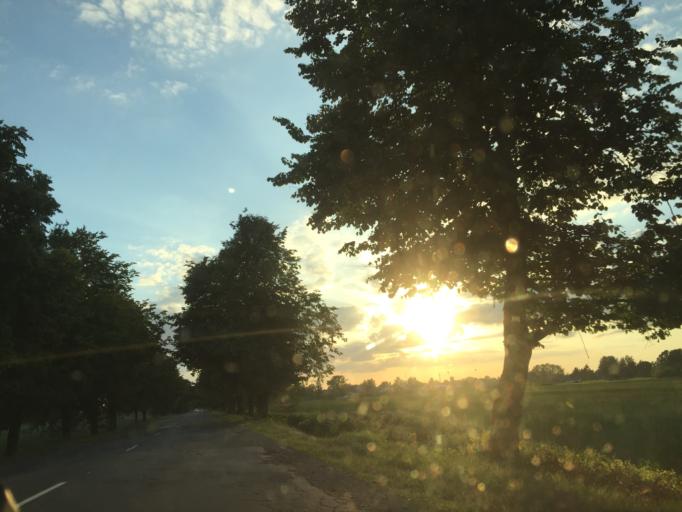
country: LV
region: Sigulda
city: Sigulda
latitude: 57.1393
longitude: 24.8770
